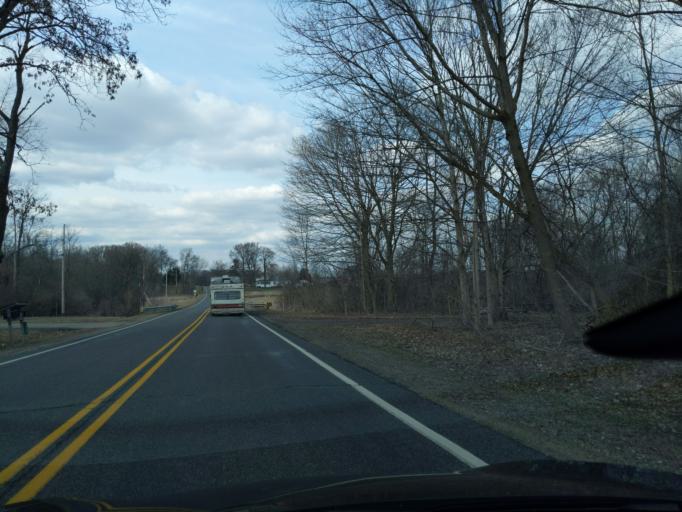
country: US
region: Michigan
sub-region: Ingham County
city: Leslie
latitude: 42.3652
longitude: -84.4201
